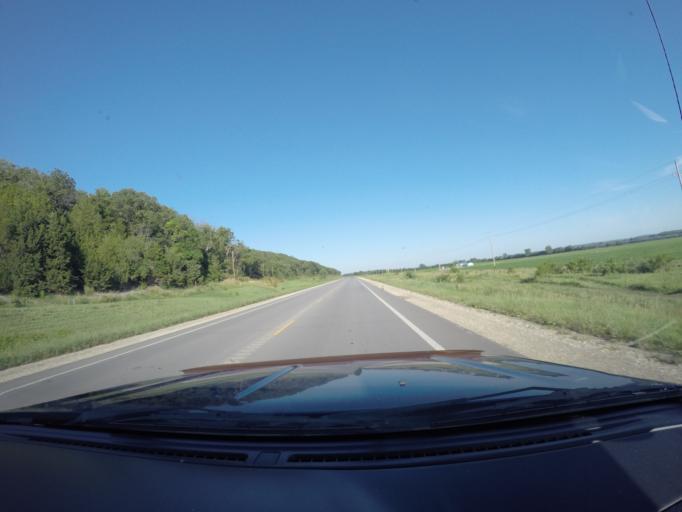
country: US
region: Kansas
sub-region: Jefferson County
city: Oskaloosa
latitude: 39.0730
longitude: -95.3626
